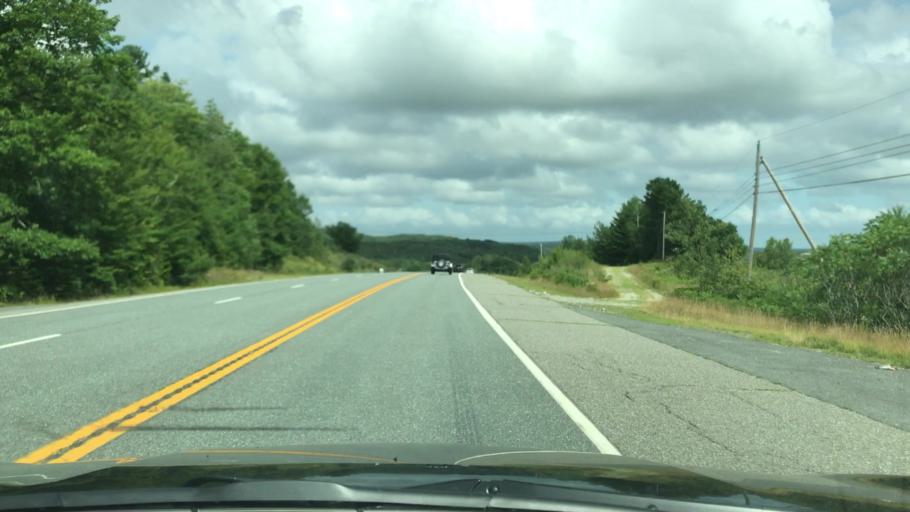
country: US
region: Maine
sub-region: Hancock County
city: Orland
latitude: 44.5679
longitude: -68.6252
